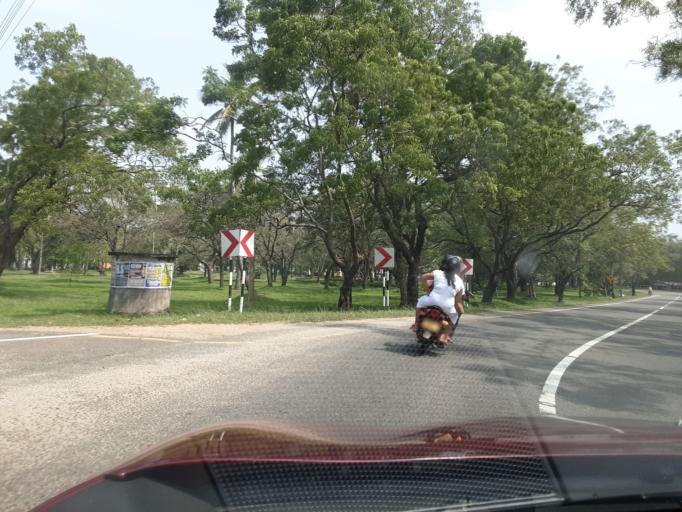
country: LK
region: North Central
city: Anuradhapura
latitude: 8.3566
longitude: 80.5106
